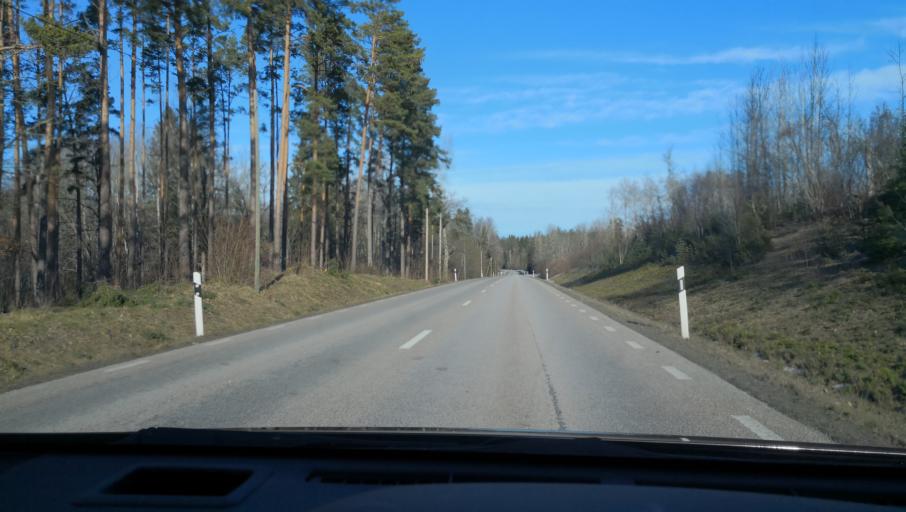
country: SE
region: Uppsala
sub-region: Osthammars Kommun
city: Osterbybruk
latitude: 60.1665
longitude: 17.8444
